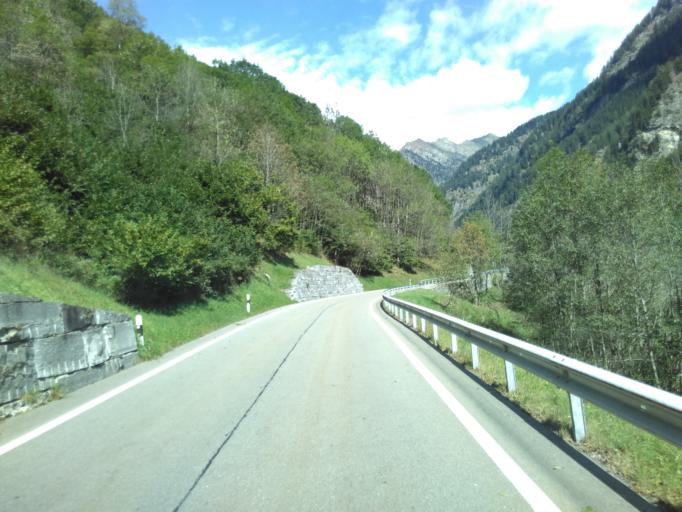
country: CH
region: Grisons
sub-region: Moesa District
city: Cauco
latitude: 46.3476
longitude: 9.1205
